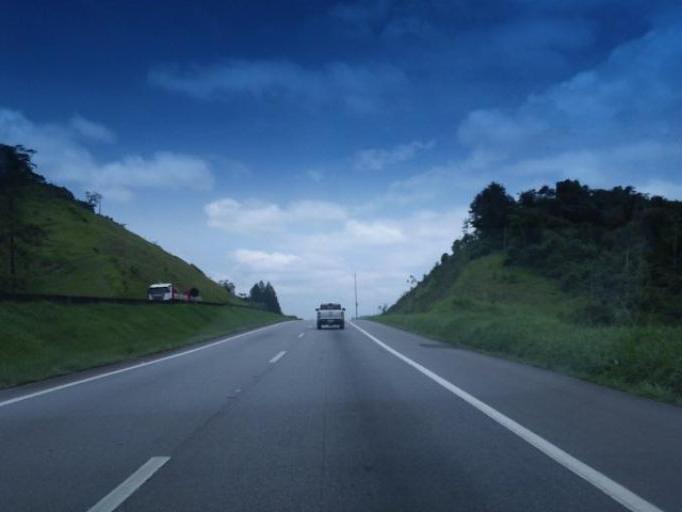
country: BR
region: Sao Paulo
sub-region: Miracatu
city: Miracatu
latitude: -24.1678
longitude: -47.3361
